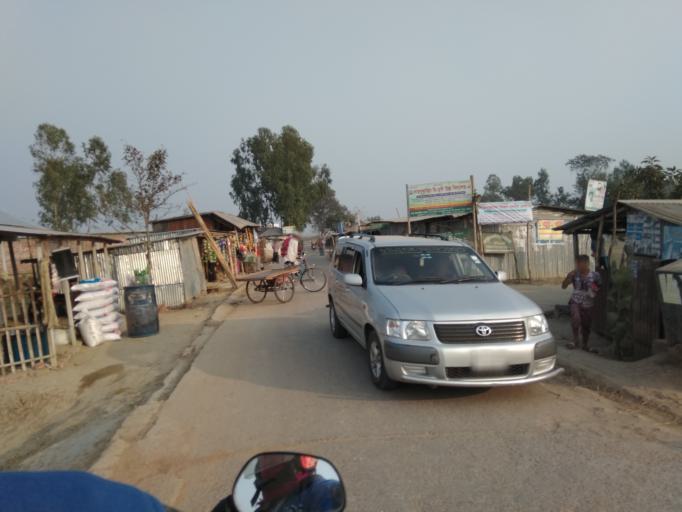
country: BD
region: Rajshahi
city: Ishurdi
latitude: 24.4930
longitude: 89.2004
